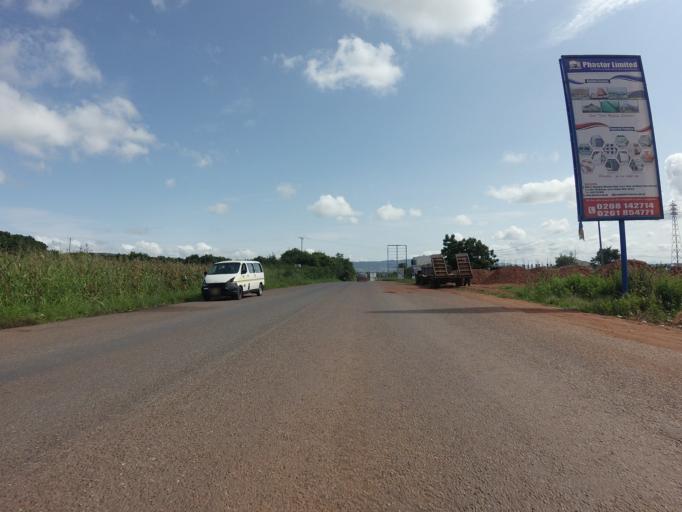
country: GH
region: Eastern
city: Aburi
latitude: 5.8247
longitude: -0.1194
